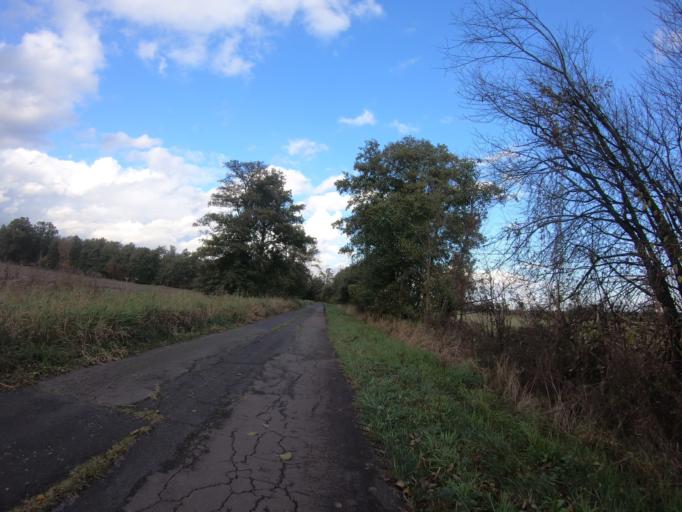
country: DE
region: Lower Saxony
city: Wagenhoff
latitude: 52.5409
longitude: 10.5549
